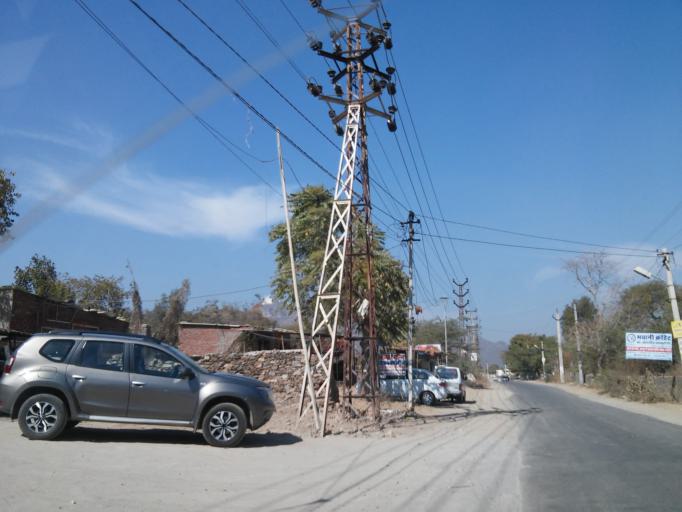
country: IN
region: Rajasthan
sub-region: Udaipur
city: Udaipur
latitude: 24.5772
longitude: 73.6552
